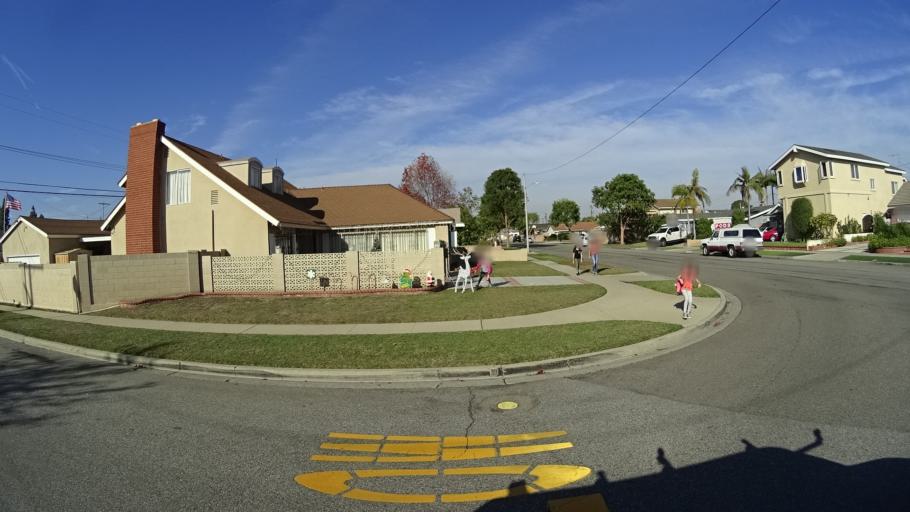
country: US
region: California
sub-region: Orange County
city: Westminster
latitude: 33.7777
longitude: -118.0233
